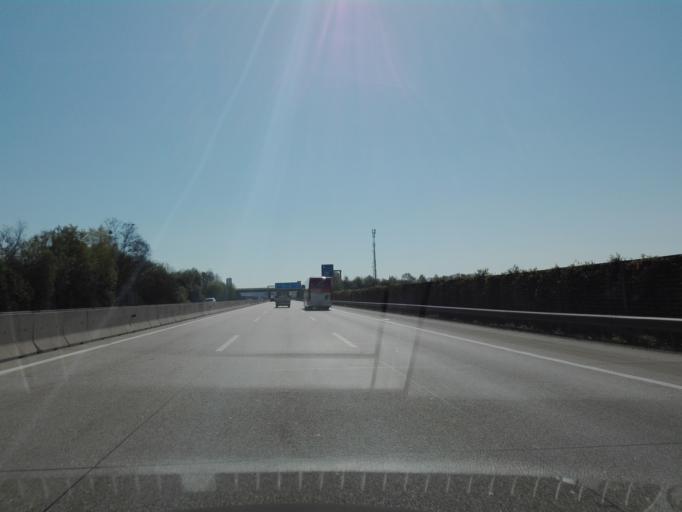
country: AT
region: Upper Austria
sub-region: Politischer Bezirk Linz-Land
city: Asten
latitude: 48.2151
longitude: 14.4157
